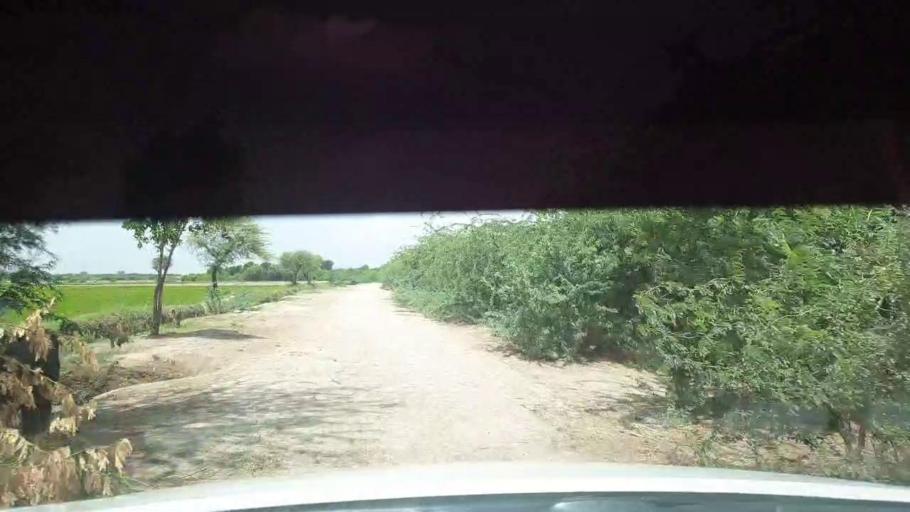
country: PK
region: Sindh
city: Kadhan
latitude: 24.5470
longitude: 68.9710
